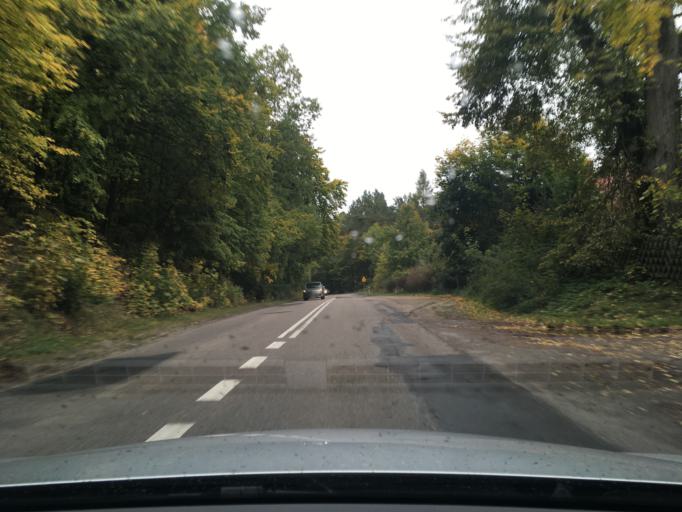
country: PL
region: Pomeranian Voivodeship
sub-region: Powiat koscierski
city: Koscierzyna
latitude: 54.0994
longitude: 17.9762
